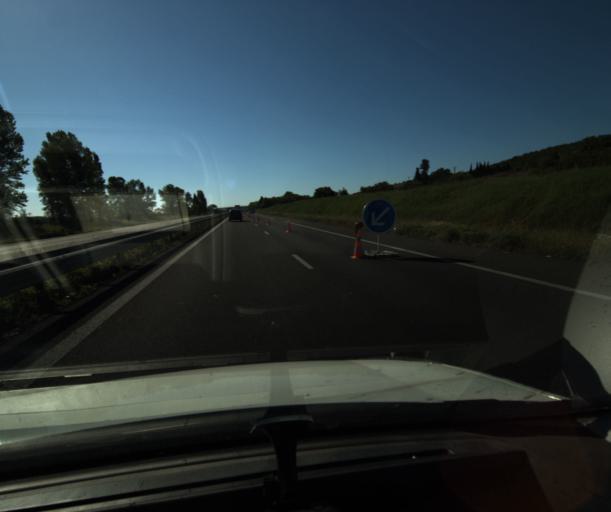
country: FR
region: Midi-Pyrenees
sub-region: Departement de la Haute-Garonne
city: Avignonet-Lauragais
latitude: 43.3348
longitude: 1.8399
